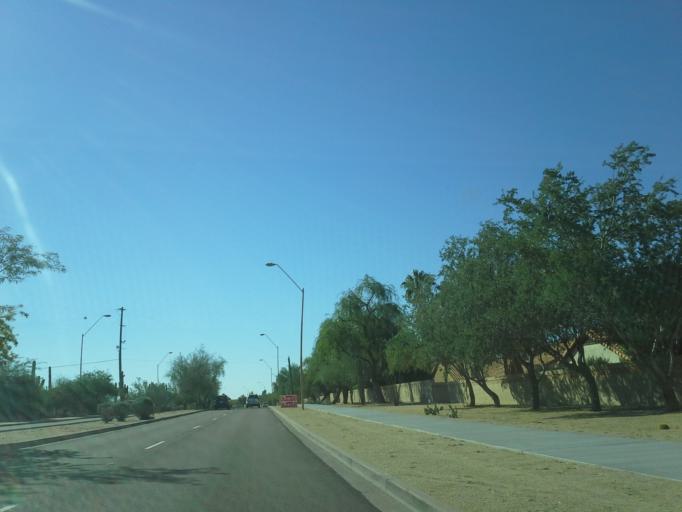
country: US
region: Arizona
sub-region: Maricopa County
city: Scottsdale
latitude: 33.6070
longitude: -111.8564
